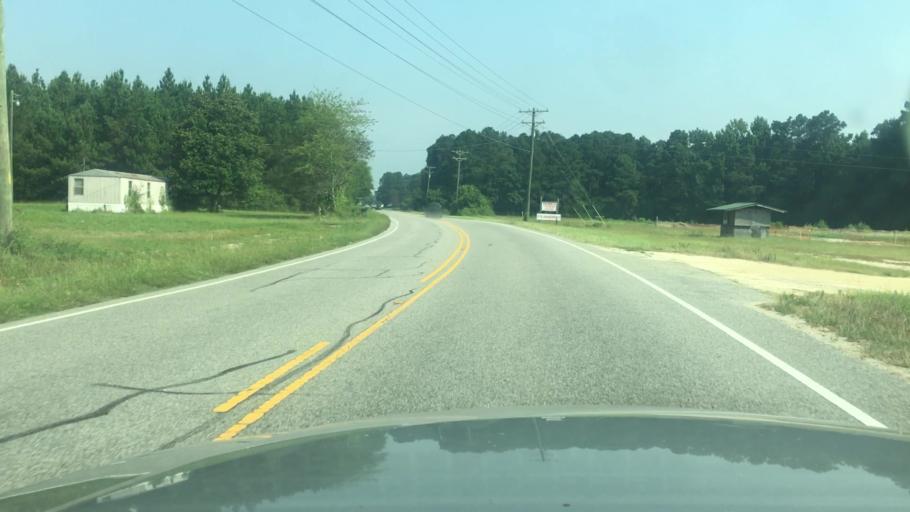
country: US
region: North Carolina
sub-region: Cumberland County
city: Hope Mills
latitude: 34.9117
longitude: -78.9054
